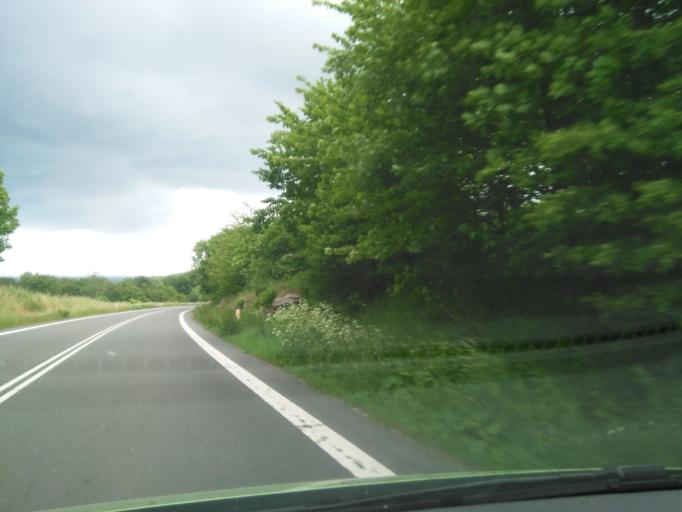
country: DK
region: Capital Region
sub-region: Bornholm Kommune
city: Akirkeby
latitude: 55.2212
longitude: 14.9026
